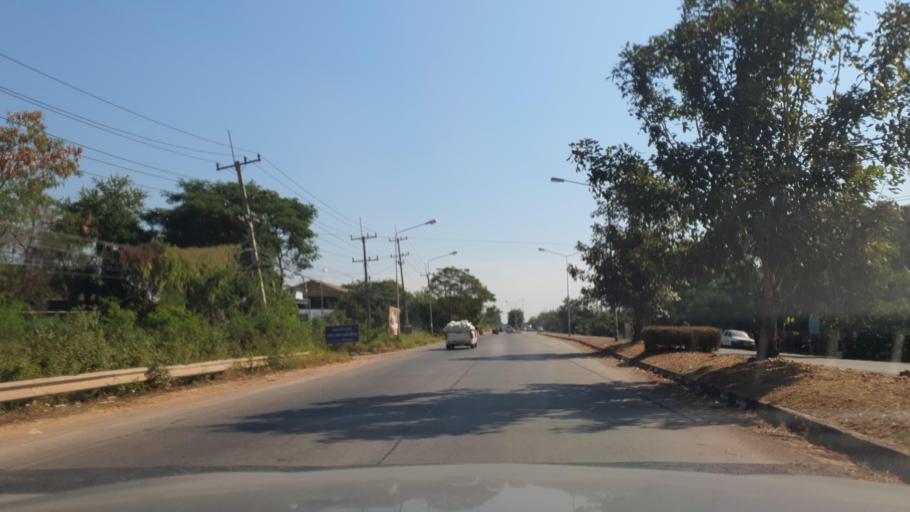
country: TH
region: Khon Kaen
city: Khon Kaen
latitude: 16.4375
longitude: 102.9018
